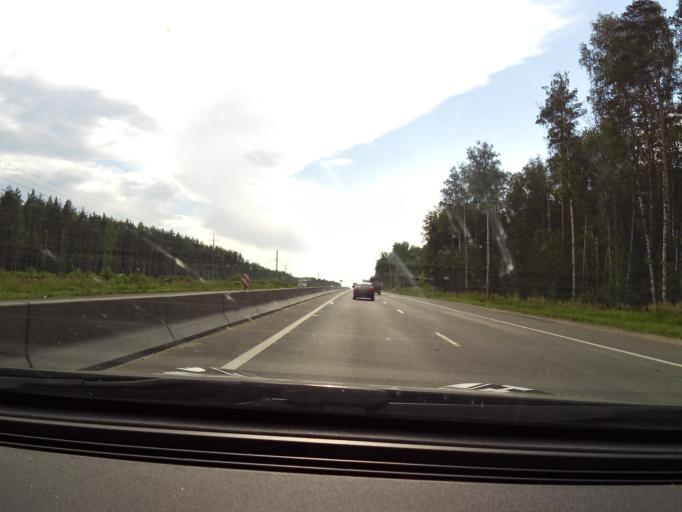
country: RU
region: Nizjnij Novgorod
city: Novosmolinskiy
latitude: 56.2807
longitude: 43.0691
